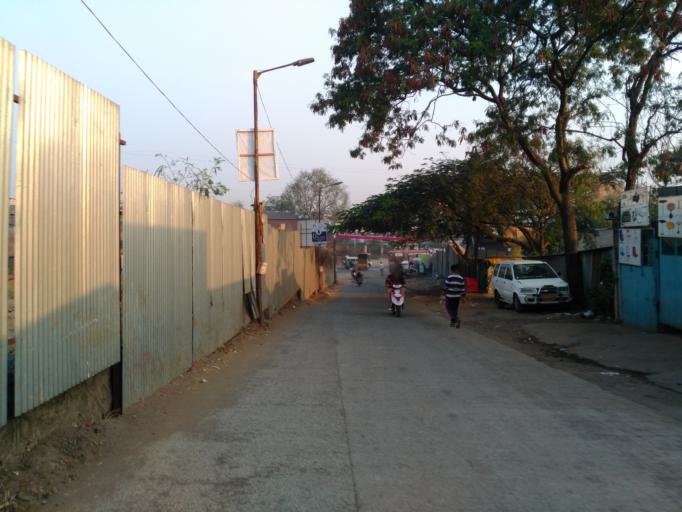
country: IN
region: Maharashtra
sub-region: Pune Division
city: Pune
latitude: 18.4497
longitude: 73.8795
